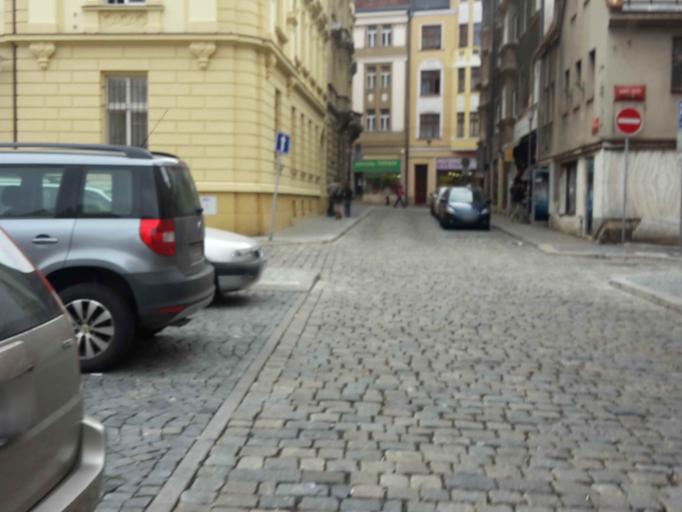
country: CZ
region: Liberecky
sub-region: Okres Liberec
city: Liberec
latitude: 50.7712
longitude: 15.0611
